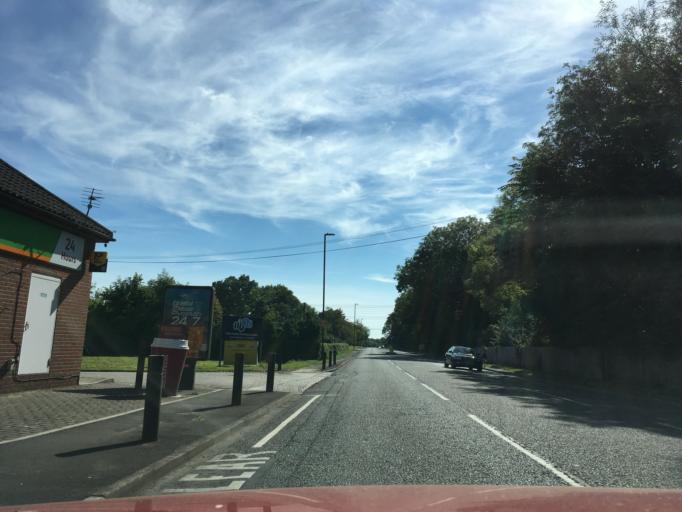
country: GB
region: England
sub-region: South Gloucestershire
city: Almondsbury
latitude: 51.5658
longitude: -2.5532
